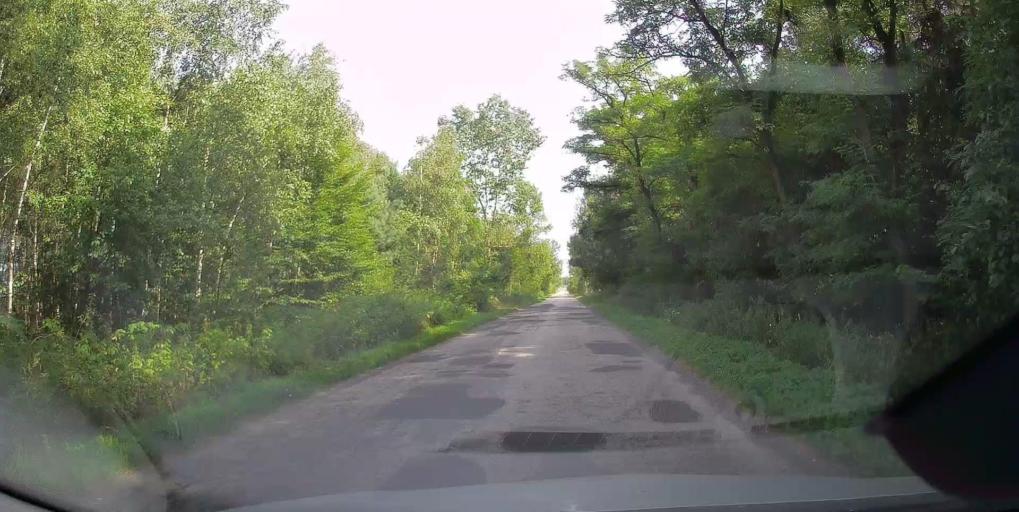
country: PL
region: Lodz Voivodeship
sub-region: Powiat opoczynski
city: Mniszkow
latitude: 51.4178
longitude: 20.0302
